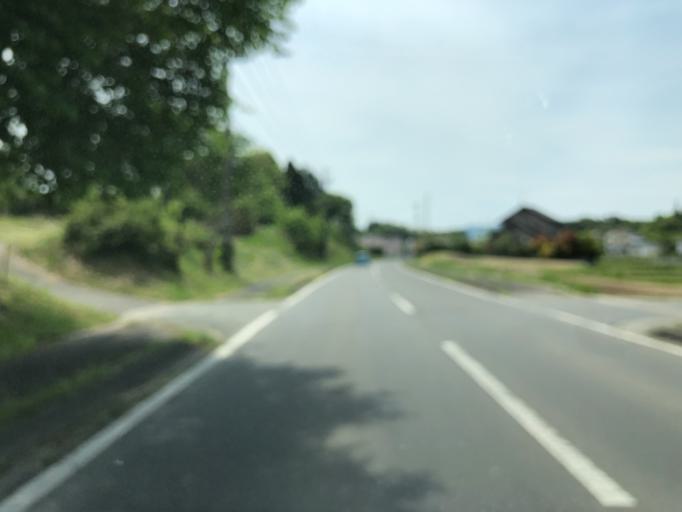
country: JP
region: Miyagi
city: Marumori
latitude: 37.8180
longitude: 140.9363
